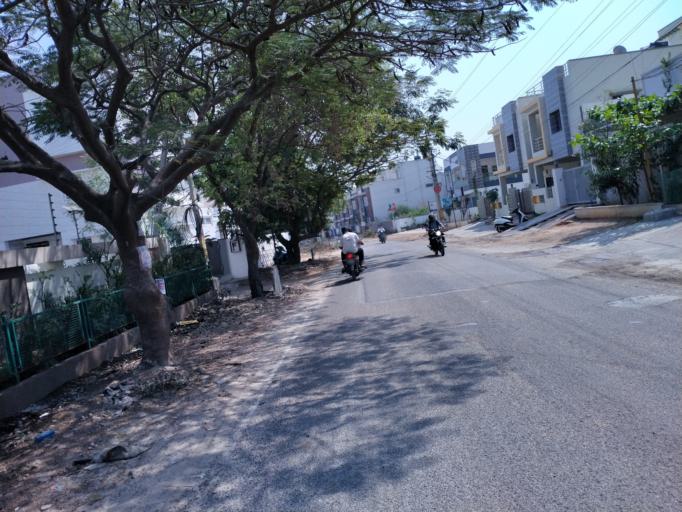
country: IN
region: Telangana
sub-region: Rangareddi
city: Secunderabad
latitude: 17.5019
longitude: 78.5492
